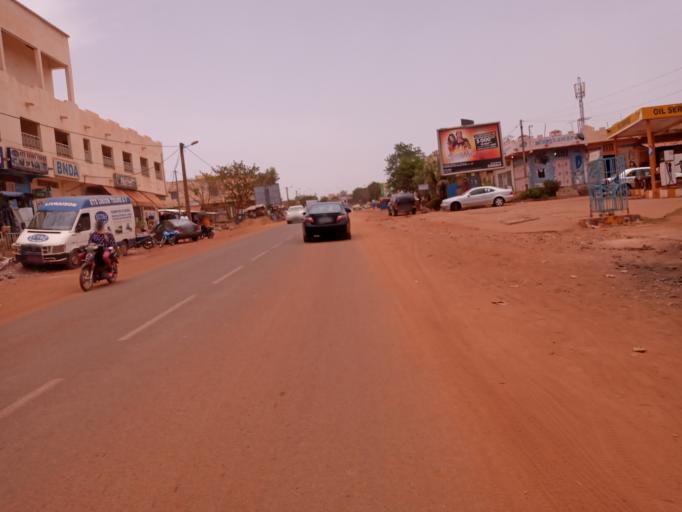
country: ML
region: Bamako
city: Bamako
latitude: 12.5749
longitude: -8.0089
